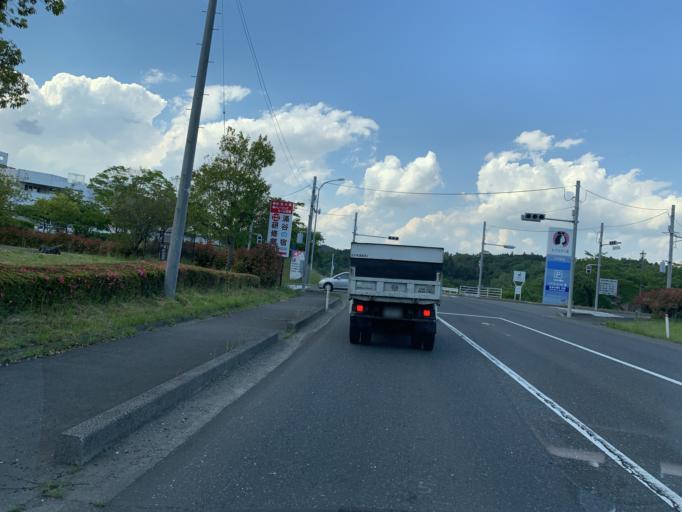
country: JP
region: Miyagi
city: Wakuya
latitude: 38.5397
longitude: 141.1500
